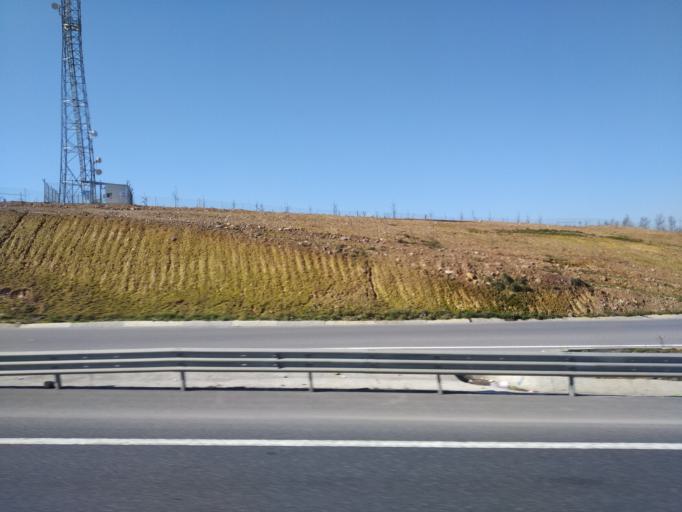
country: TR
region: Istanbul
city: Sancaktepe
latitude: 41.0996
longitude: 29.2899
